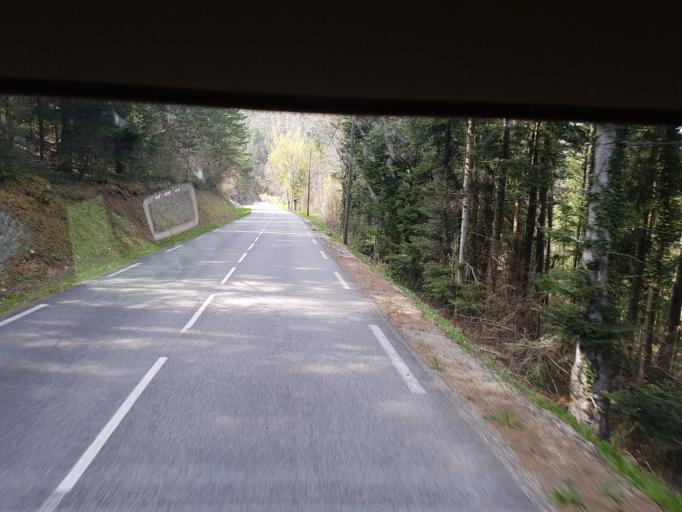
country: FR
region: Languedoc-Roussillon
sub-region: Departement de la Lozere
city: Florac
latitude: 44.3017
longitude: 3.5999
